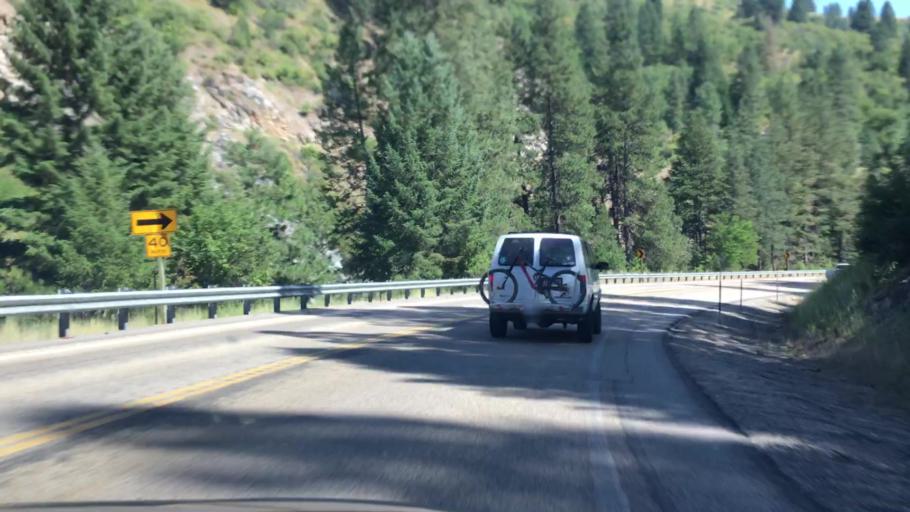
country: US
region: Idaho
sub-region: Valley County
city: Cascade
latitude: 44.1301
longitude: -116.1118
